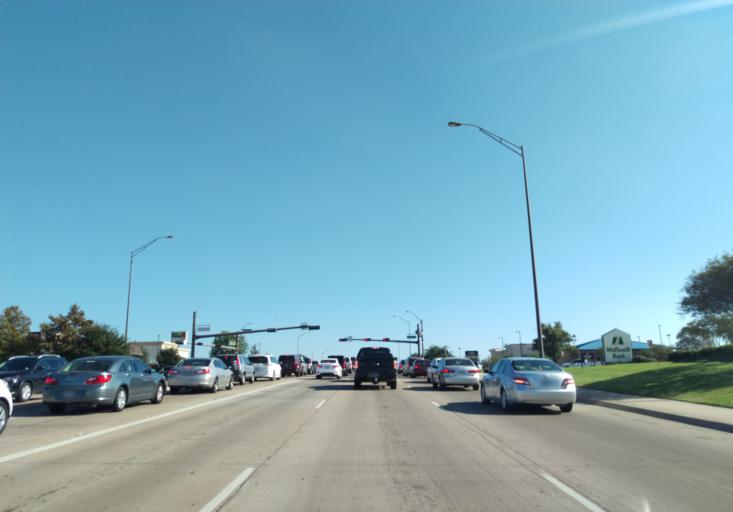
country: US
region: Texas
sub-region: Brazos County
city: College Station
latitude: 30.6133
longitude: -96.3168
